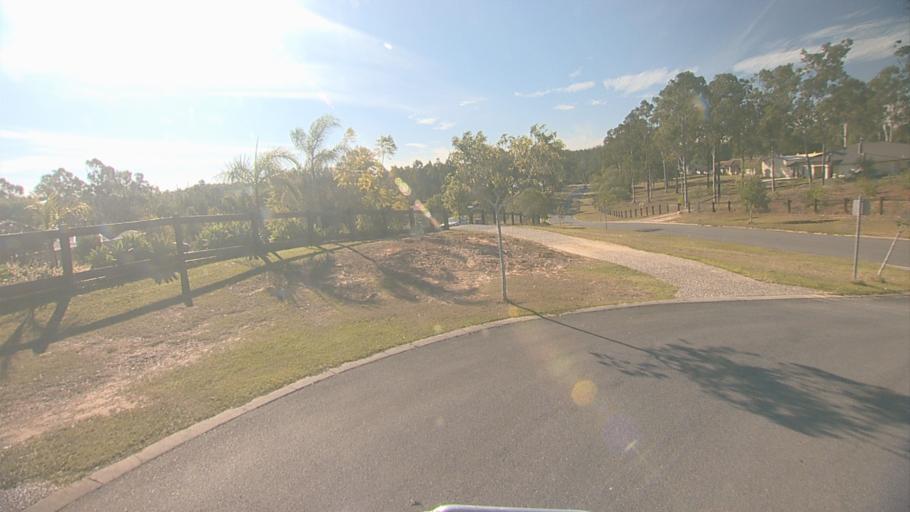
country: AU
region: Queensland
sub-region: Ipswich
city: Springfield Lakes
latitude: -27.7191
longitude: 152.9202
